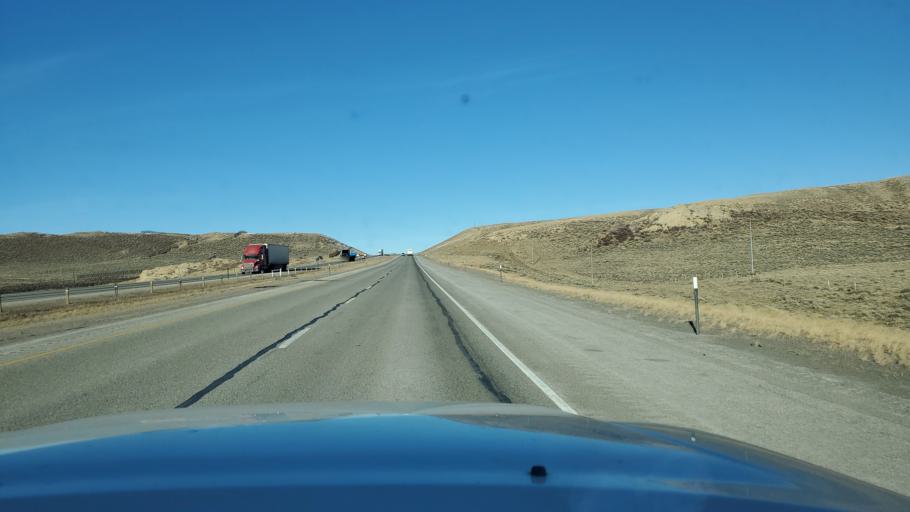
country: US
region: Wyoming
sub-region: Carbon County
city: Saratoga
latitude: 41.7492
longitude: -106.5033
